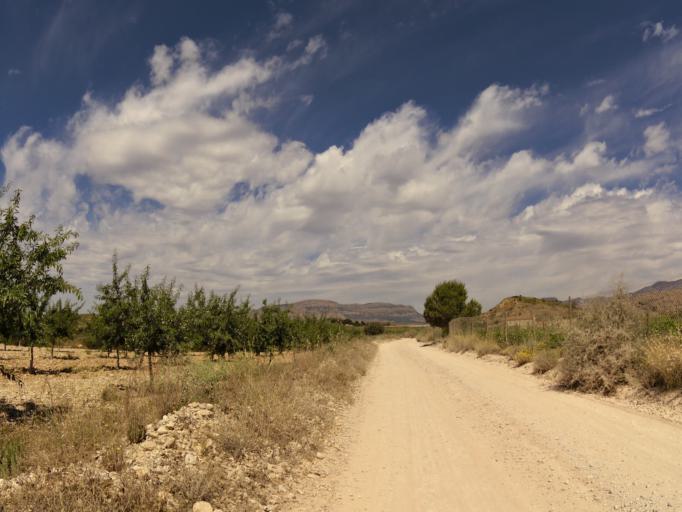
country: ES
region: Valencia
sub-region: Provincia de Alicante
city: Agost
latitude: 38.4049
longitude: -0.6126
